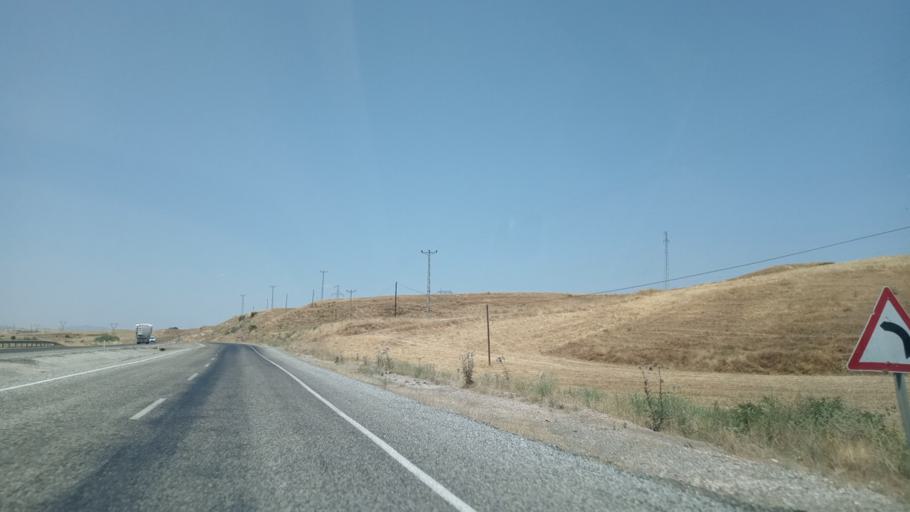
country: TR
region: Batman
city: Bekirhan
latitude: 38.1573
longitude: 41.3466
